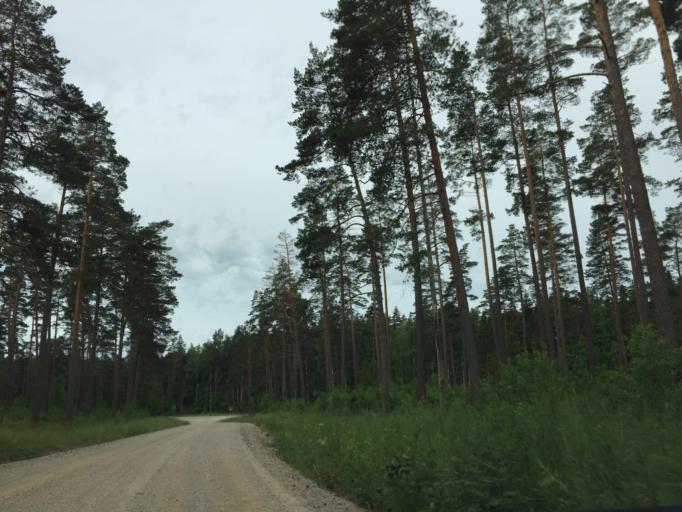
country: LV
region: Tukuma Rajons
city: Tukums
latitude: 56.9989
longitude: 23.1489
